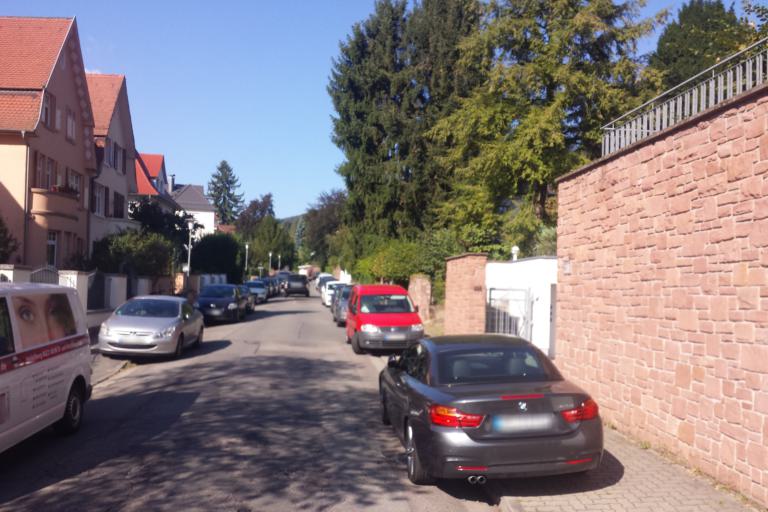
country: DE
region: Baden-Wuerttemberg
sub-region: Karlsruhe Region
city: Heidelberg
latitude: 49.4240
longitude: 8.6910
